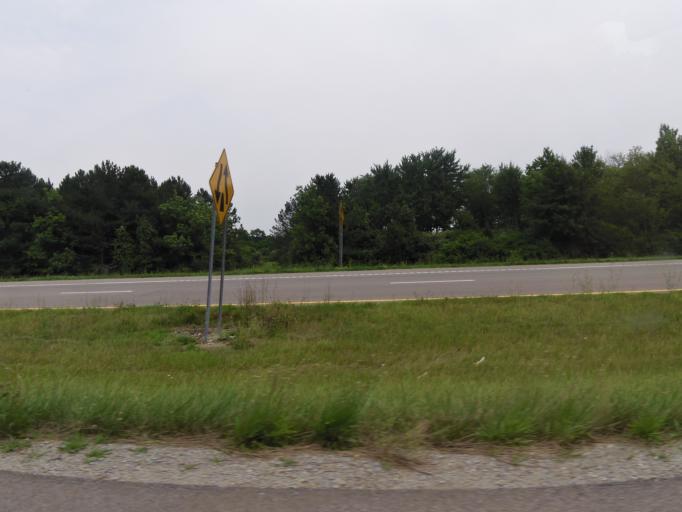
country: US
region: Ohio
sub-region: Warren County
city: Waynesville
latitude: 39.5116
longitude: -84.0280
